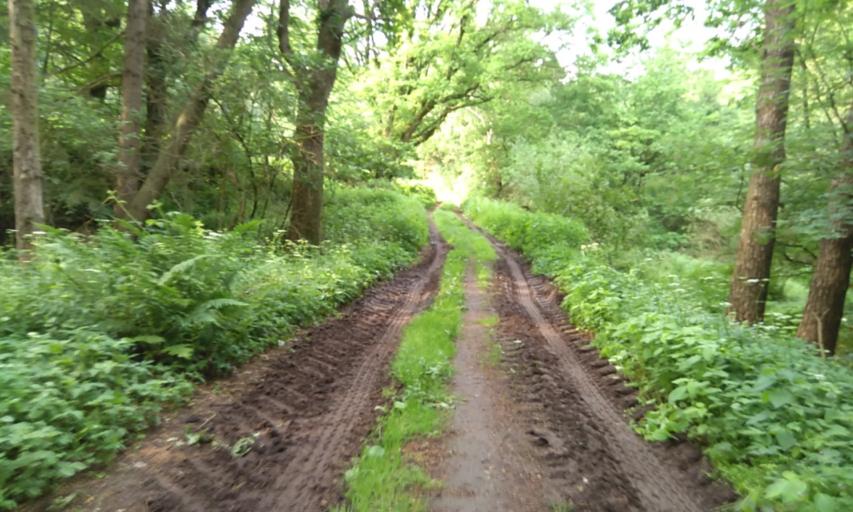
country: DE
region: Lower Saxony
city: Nottensdorf
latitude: 53.4689
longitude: 9.6221
